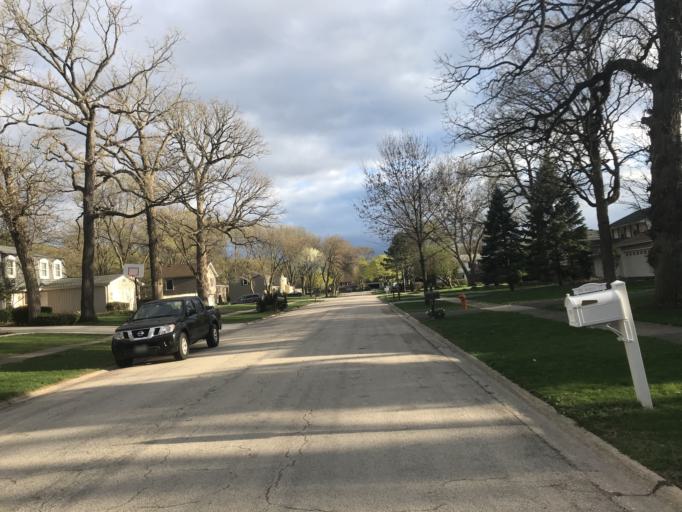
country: US
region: Illinois
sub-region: DuPage County
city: Naperville
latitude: 41.7366
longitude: -88.1168
